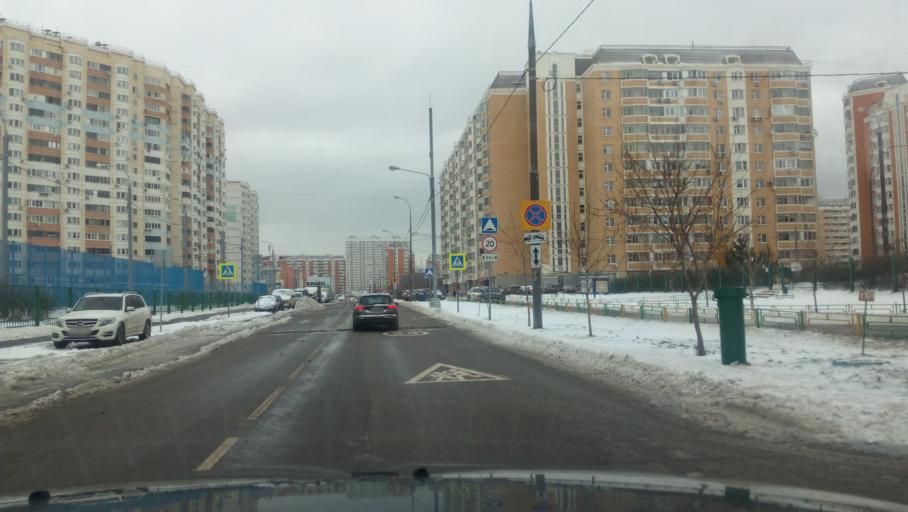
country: RU
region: Moscow
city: Nekrasovka
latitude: 55.7101
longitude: 37.8858
